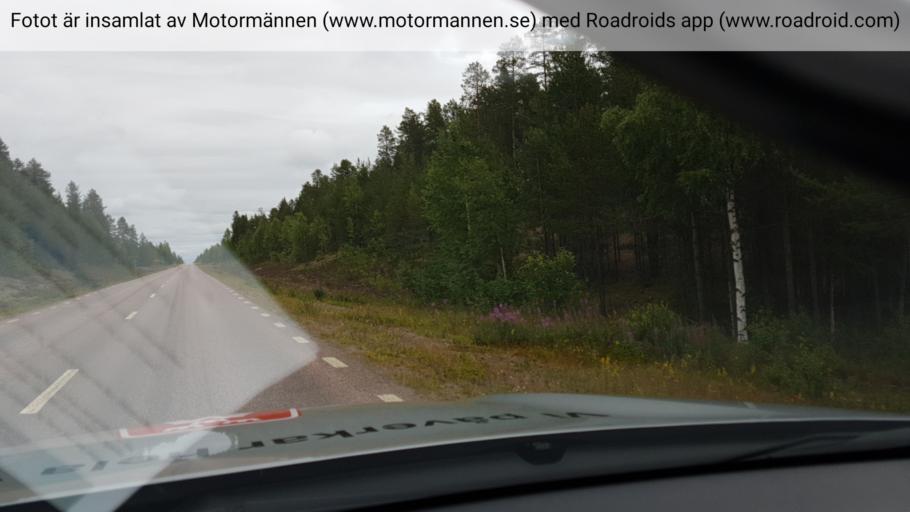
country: SE
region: Norrbotten
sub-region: Overkalix Kommun
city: OEverkalix
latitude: 67.0803
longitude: 22.5396
